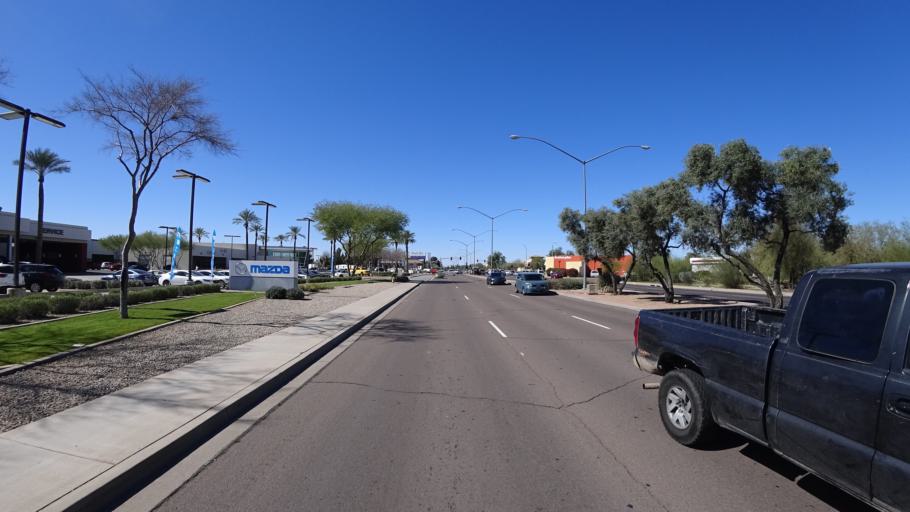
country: US
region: Arizona
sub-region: Maricopa County
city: San Carlos
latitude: 33.3787
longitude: -111.8395
